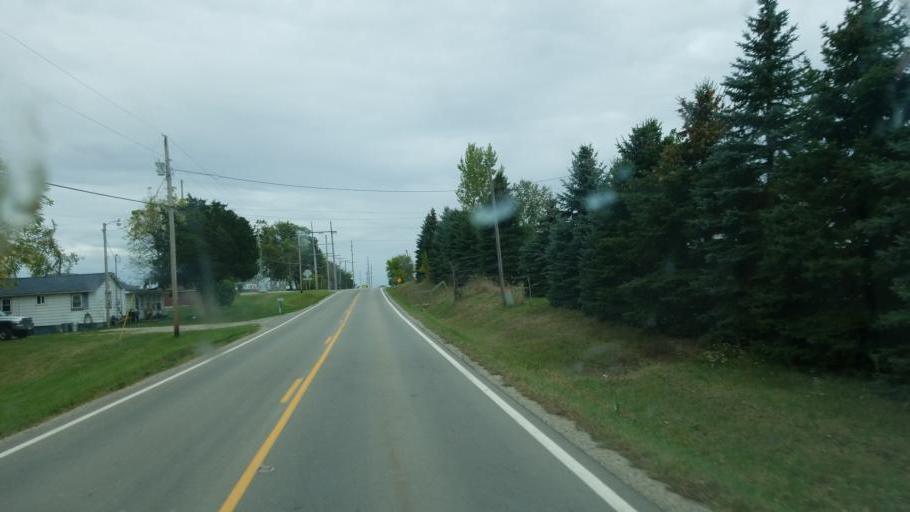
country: US
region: Ohio
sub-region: Huron County
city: New London
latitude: 41.1150
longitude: -82.4092
